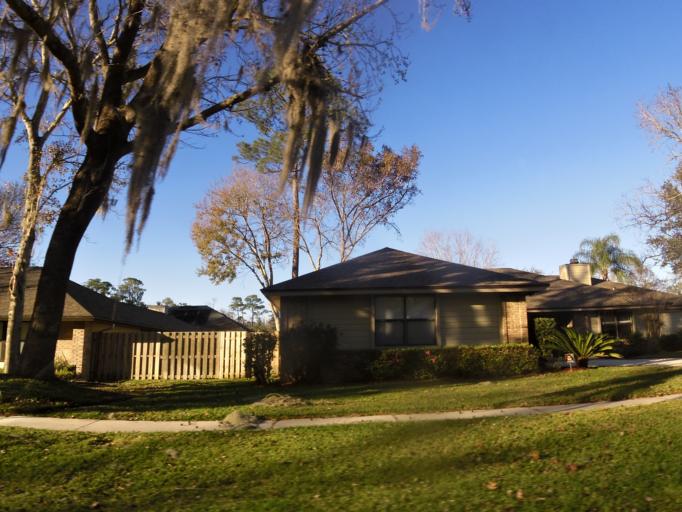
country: US
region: Florida
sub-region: Saint Johns County
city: Fruit Cove
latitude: 30.2114
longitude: -81.6080
